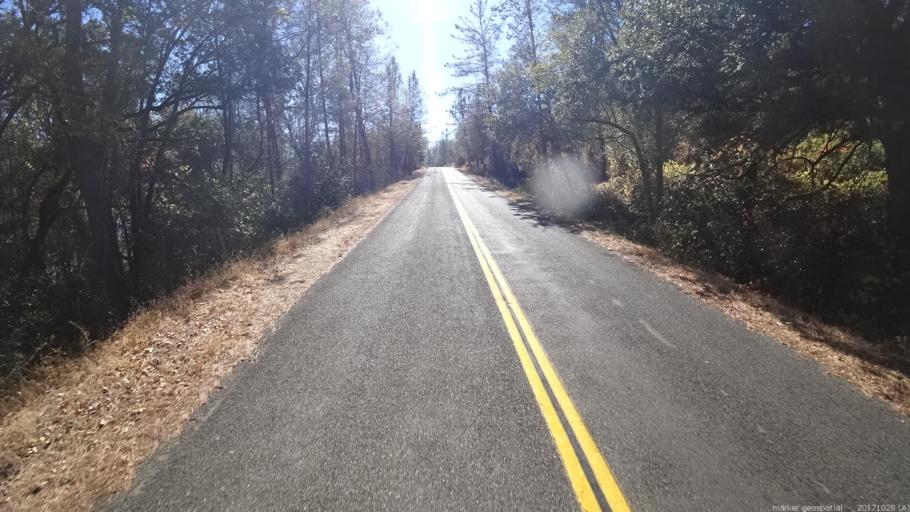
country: US
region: California
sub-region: Shasta County
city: Shasta
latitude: 40.6479
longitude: -122.5579
